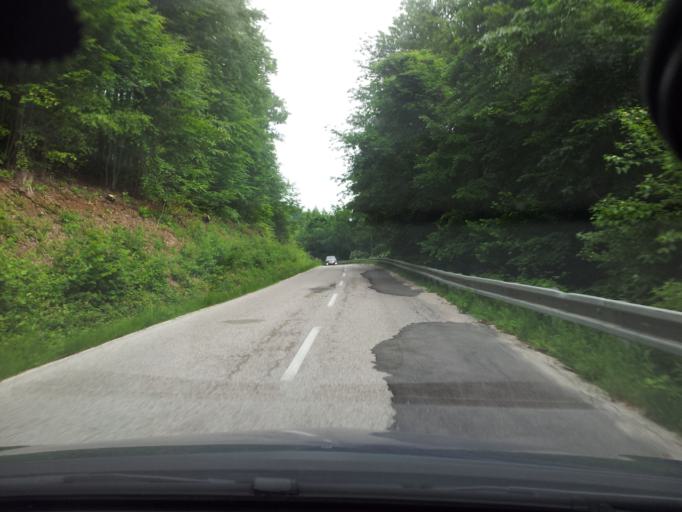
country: SK
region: Nitriansky
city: Partizanske
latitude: 48.5693
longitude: 18.4569
